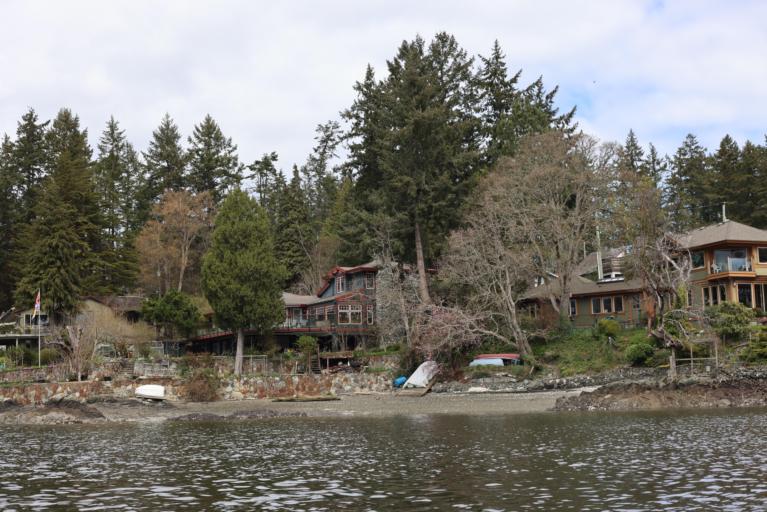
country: CA
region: British Columbia
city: North Saanich
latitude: 48.5783
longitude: -123.4695
